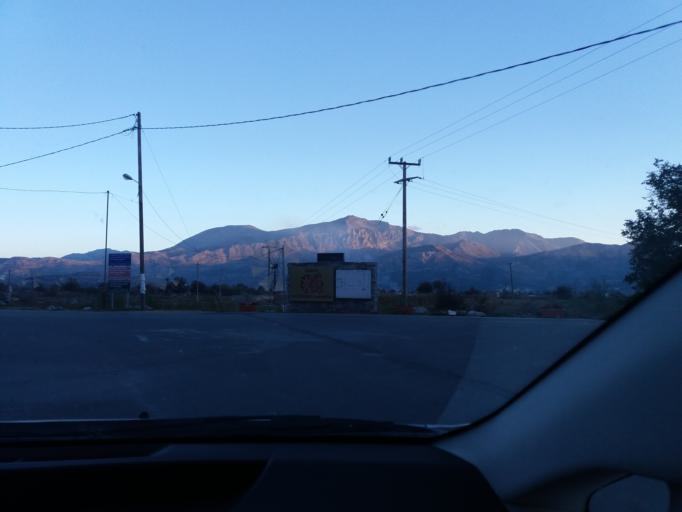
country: GR
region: Crete
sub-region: Nomos Irakleiou
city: Mokhos
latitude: 35.1969
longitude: 25.4627
